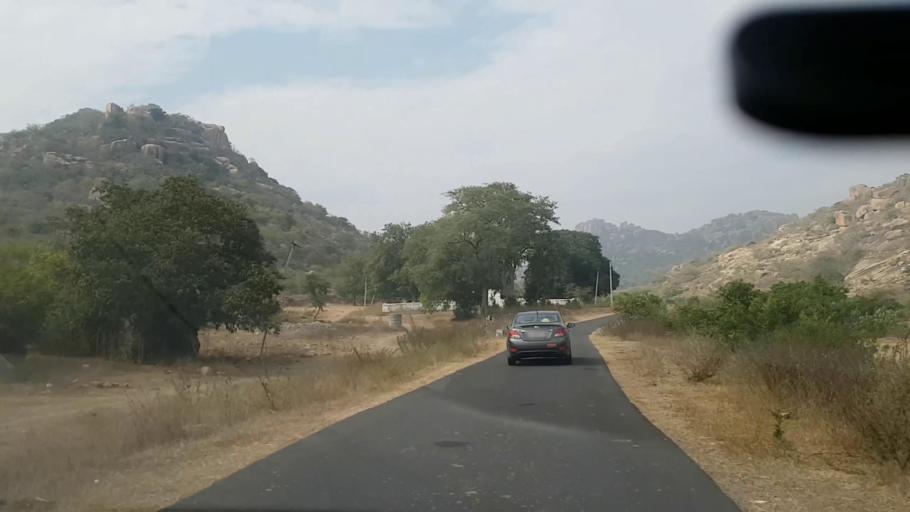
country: IN
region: Telangana
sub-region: Rangareddi
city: Ghatkesar
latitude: 17.1720
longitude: 78.8136
